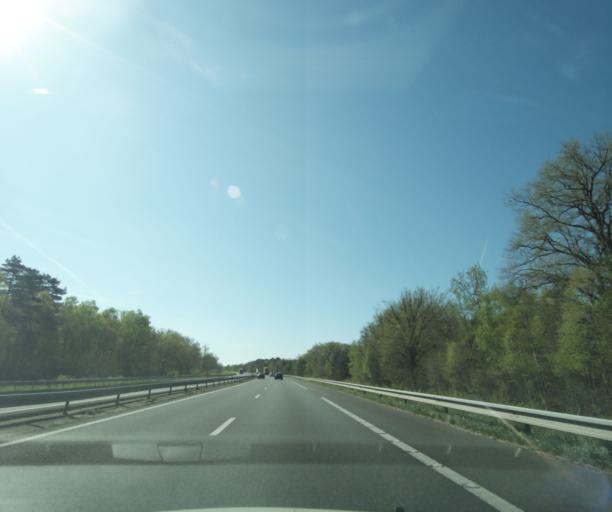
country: FR
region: Centre
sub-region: Departement du Loir-et-Cher
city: Nouan-le-Fuzelier
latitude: 47.5281
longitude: 2.0034
